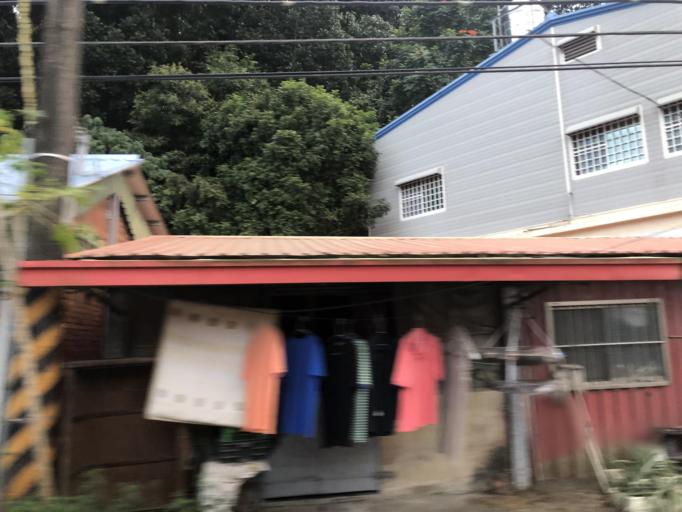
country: TW
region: Taiwan
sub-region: Tainan
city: Tainan
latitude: 23.0239
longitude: 120.3513
